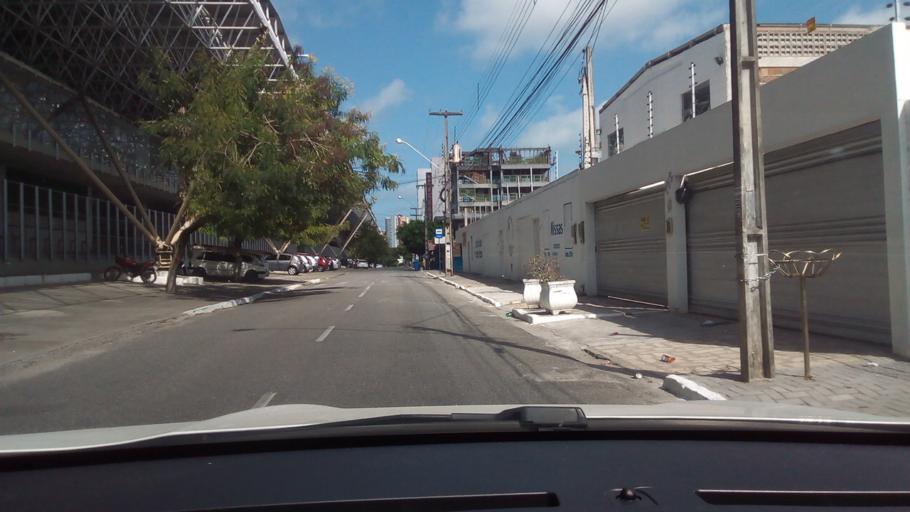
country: BR
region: Paraiba
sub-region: Joao Pessoa
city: Joao Pessoa
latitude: -7.1229
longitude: -34.8441
